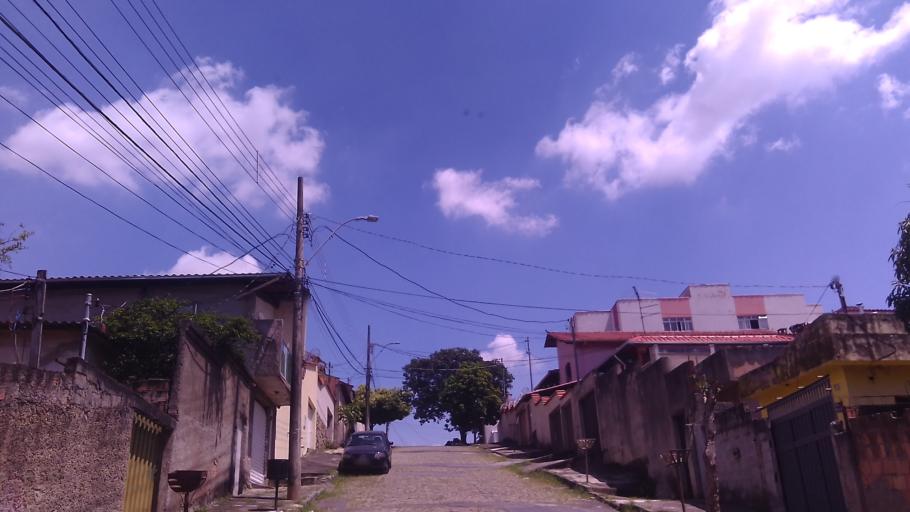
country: BR
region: Minas Gerais
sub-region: Belo Horizonte
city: Belo Horizonte
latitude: -19.8606
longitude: -43.9036
